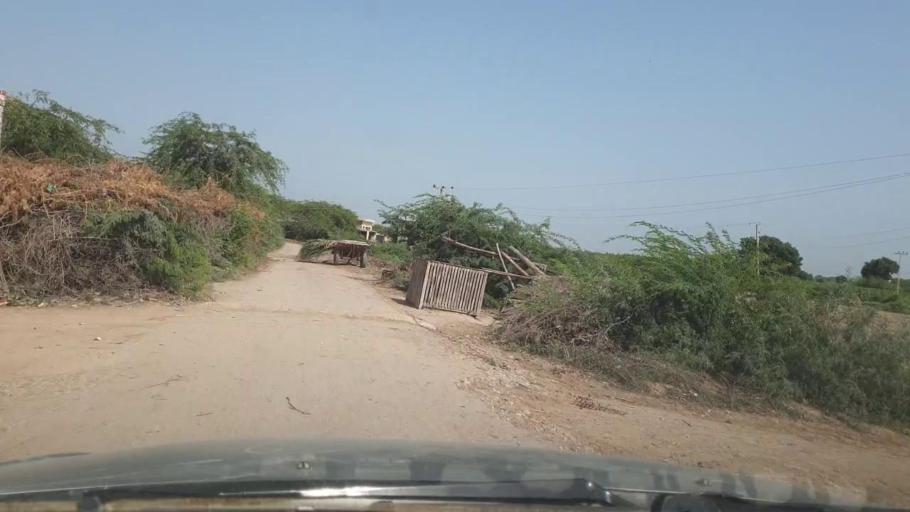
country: PK
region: Sindh
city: Tando Ghulam Ali
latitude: 25.1804
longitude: 68.8808
